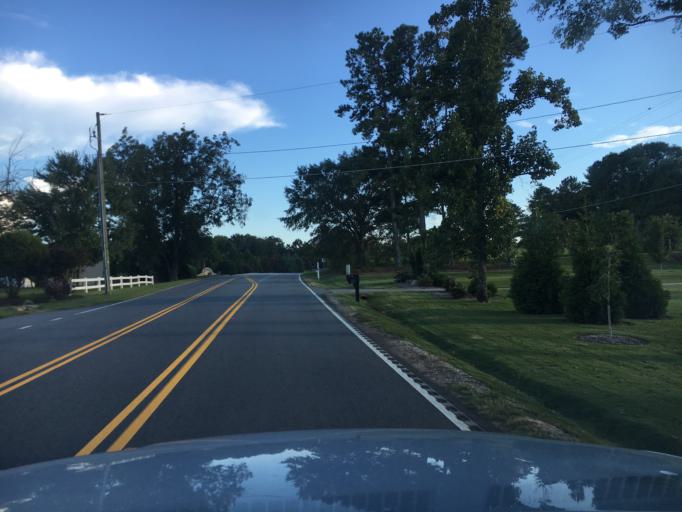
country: US
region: South Carolina
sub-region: Spartanburg County
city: Roebuck
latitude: 34.8945
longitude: -82.0070
